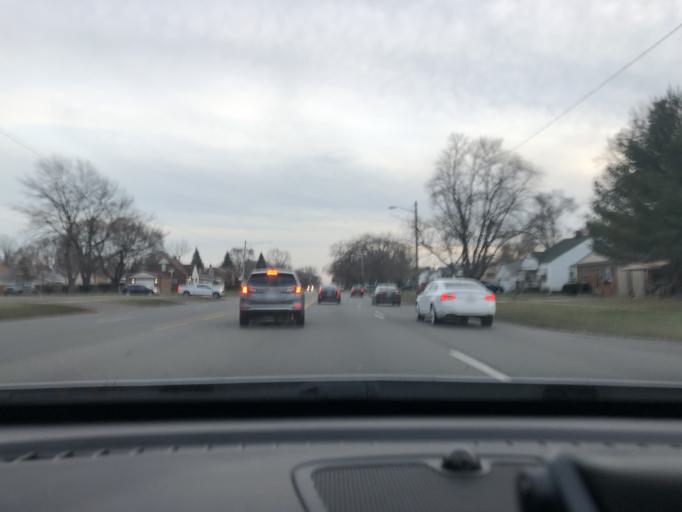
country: US
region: Michigan
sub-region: Wayne County
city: Allen Park
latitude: 42.2548
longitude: -83.2312
